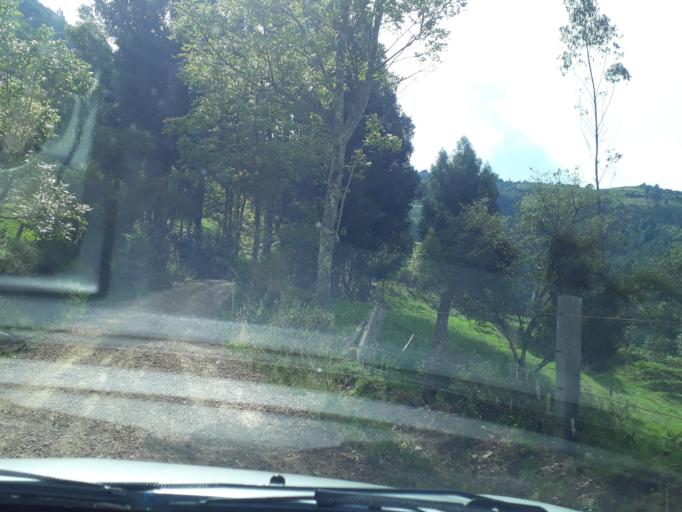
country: CO
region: Boyaca
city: Santa Rosa de Viterbo
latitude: 5.8543
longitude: -72.9672
